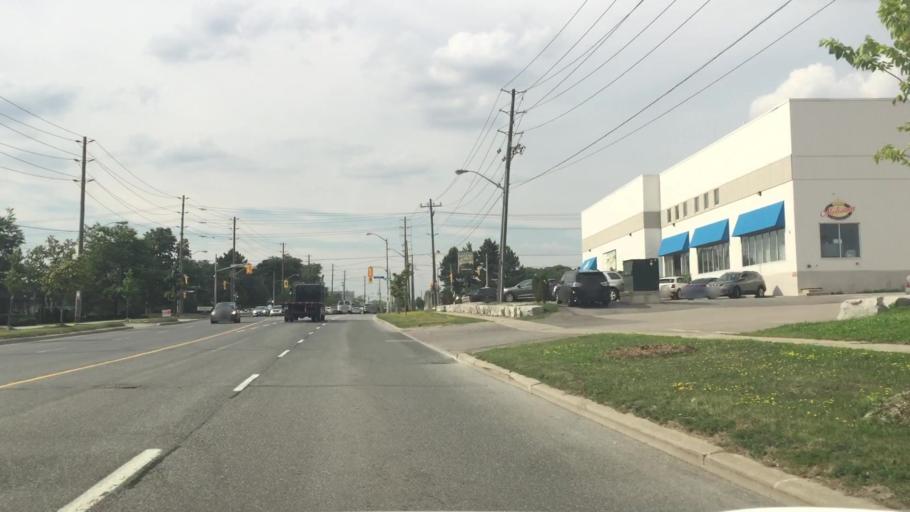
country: CA
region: Ontario
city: Concord
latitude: 43.7575
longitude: -79.5383
